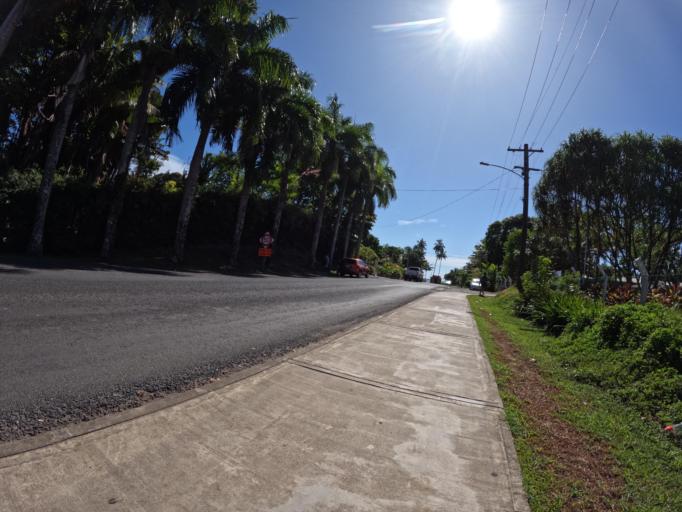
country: FJ
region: Central
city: Suva
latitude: -18.1490
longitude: 178.4528
